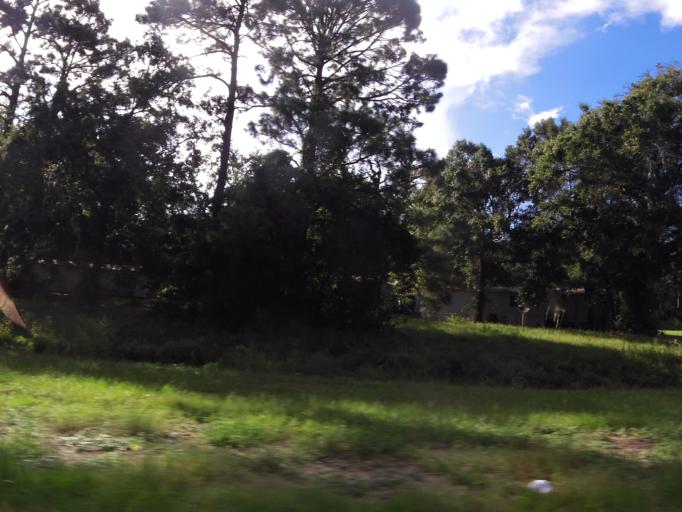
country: US
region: Georgia
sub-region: Glynn County
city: Country Club Estates
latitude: 31.2490
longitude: -81.4468
